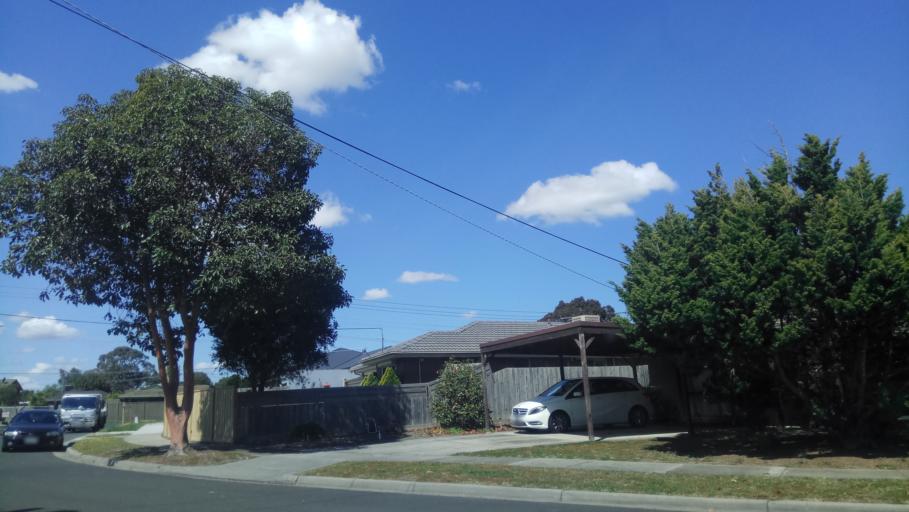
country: AU
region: Victoria
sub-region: Kingston
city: Dingley Village
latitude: -37.9847
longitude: 145.1199
